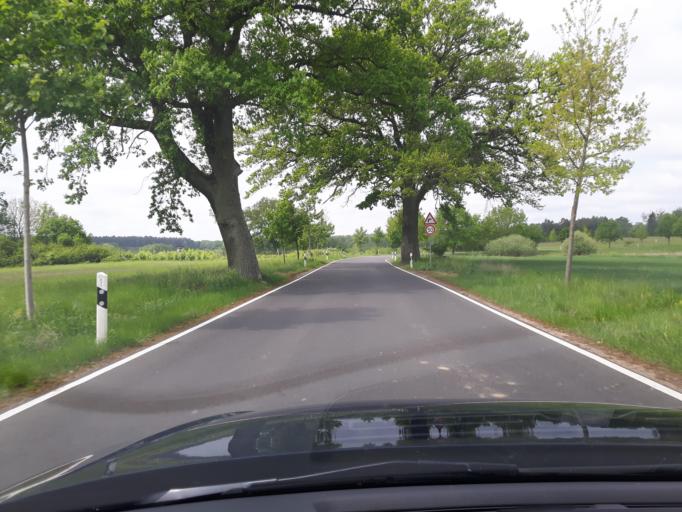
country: DE
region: Mecklenburg-Vorpommern
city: Grabowhofe
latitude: 53.5791
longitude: 12.5119
